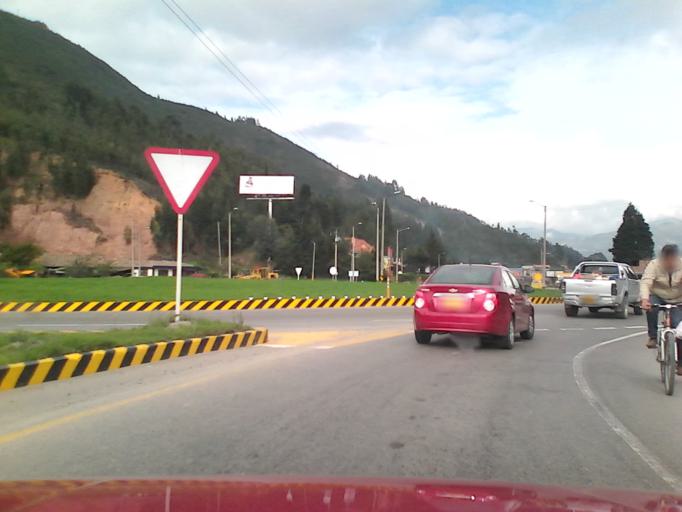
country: CO
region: Boyaca
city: Tibasosa
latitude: 5.7950
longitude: -72.9964
